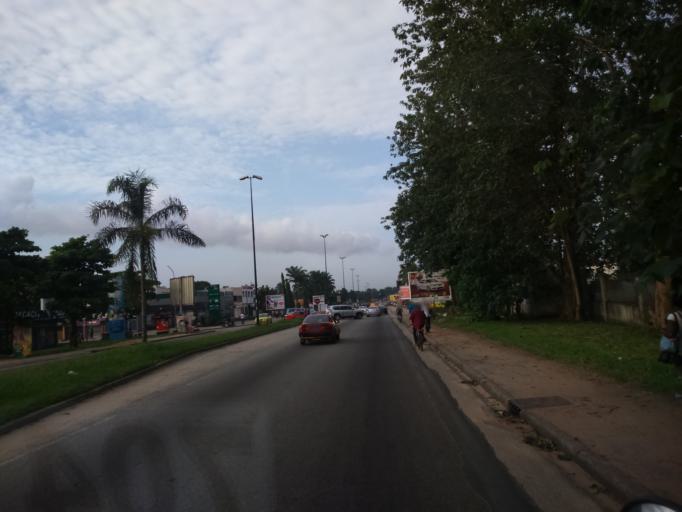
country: CI
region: Lagunes
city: Abobo
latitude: 5.3659
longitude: -3.9976
